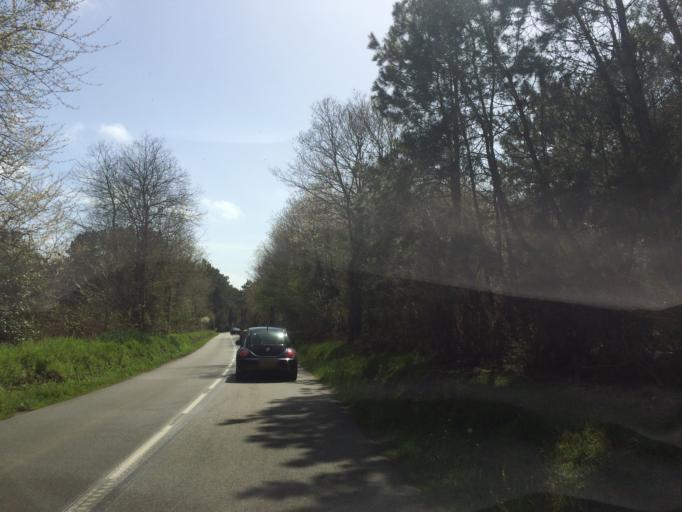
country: FR
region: Brittany
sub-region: Departement du Morbihan
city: Ploemel
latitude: 47.6303
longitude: -3.0494
